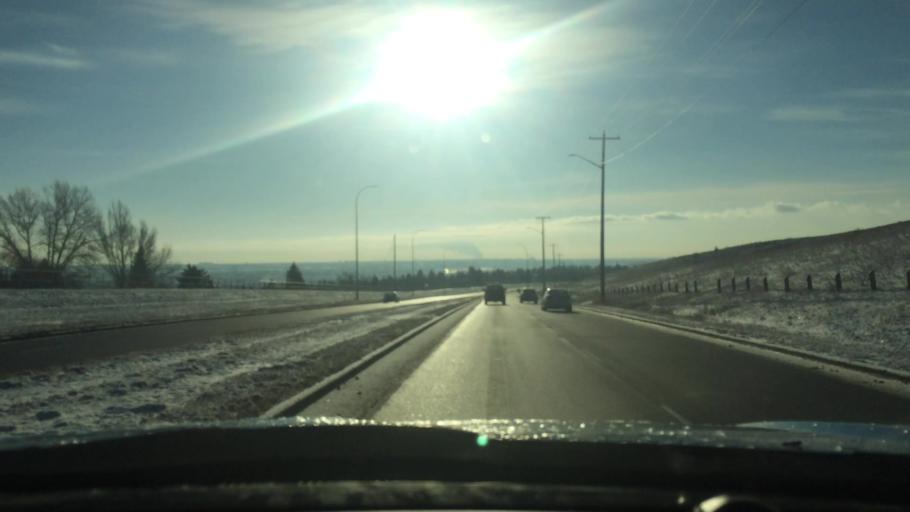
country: CA
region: Alberta
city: Calgary
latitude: 51.1191
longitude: -114.0890
